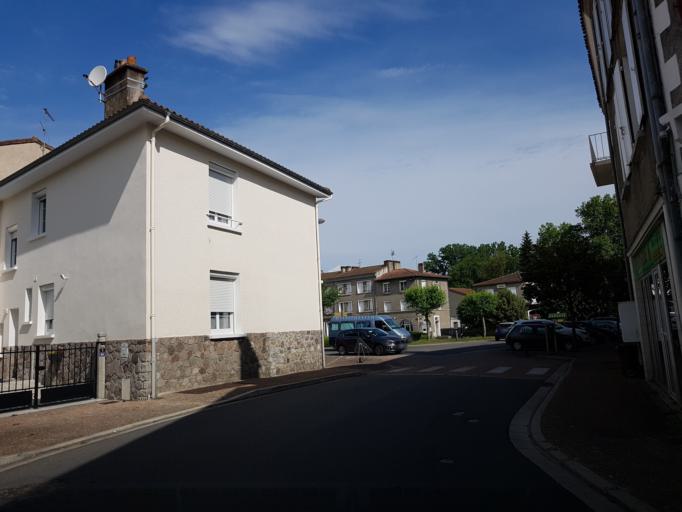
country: FR
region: Poitou-Charentes
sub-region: Departement de la Charente
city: Chabanais
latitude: 45.8730
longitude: 0.7185
